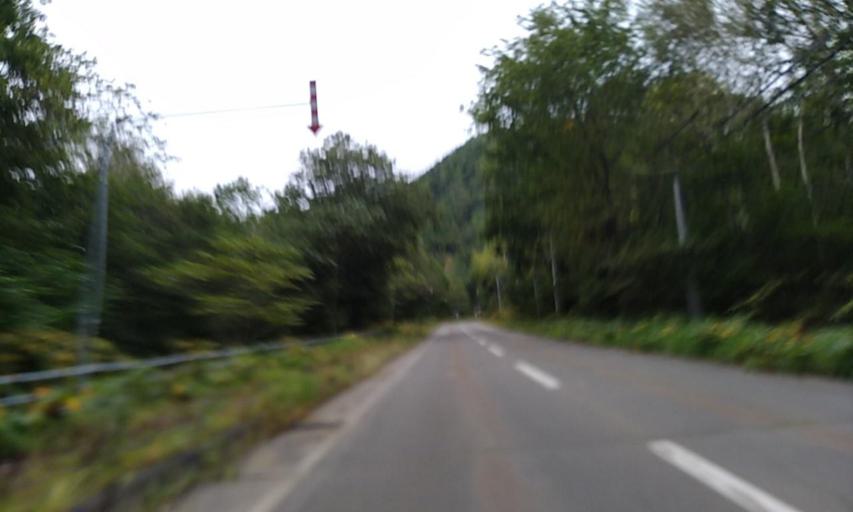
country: JP
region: Hokkaido
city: Obihiro
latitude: 42.6748
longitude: 143.0406
